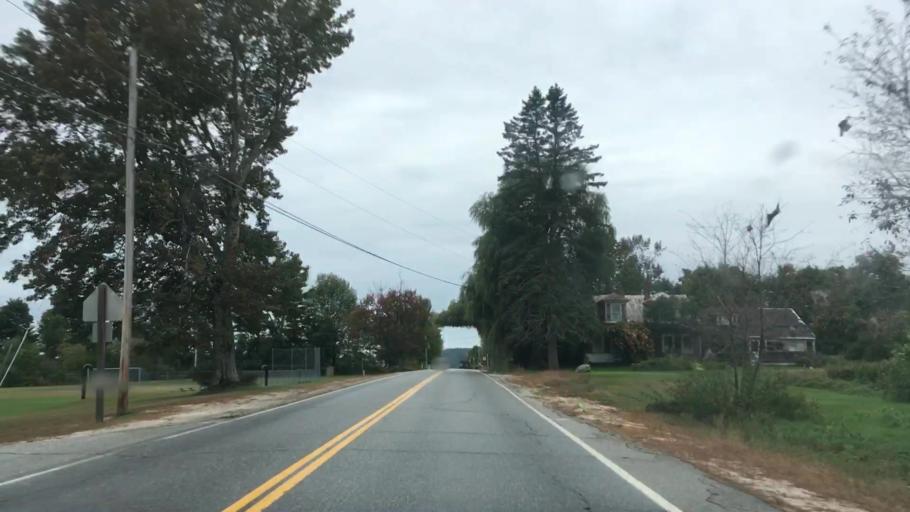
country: US
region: Maine
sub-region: Cumberland County
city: Raymond
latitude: 43.9375
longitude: -70.4468
